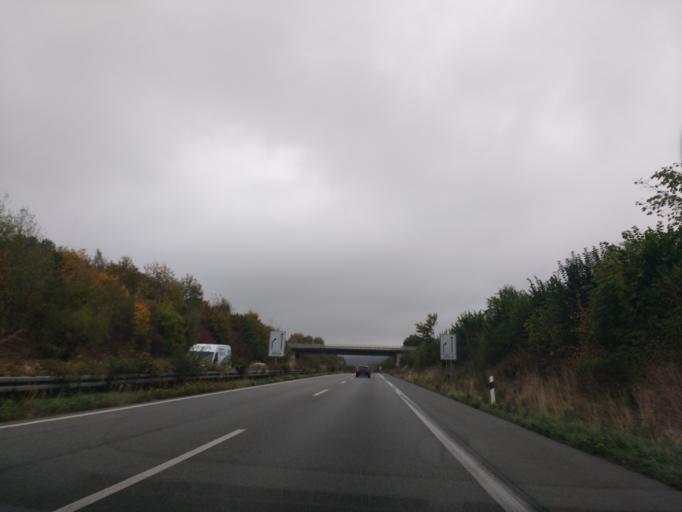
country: DE
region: Lower Saxony
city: Bissendorf
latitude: 52.1876
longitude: 8.1476
